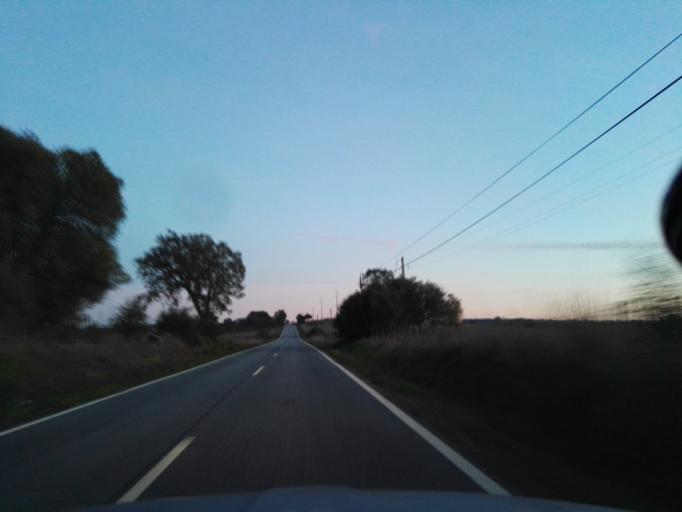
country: PT
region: Evora
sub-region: Arraiolos
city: Arraiolos
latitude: 38.7219
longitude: -8.0548
